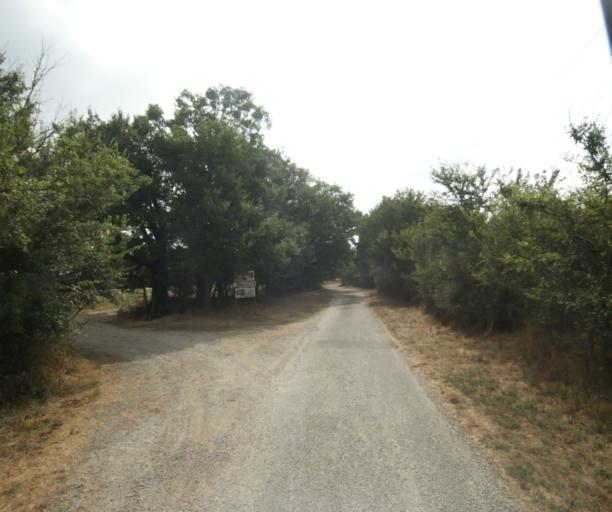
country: FR
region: Midi-Pyrenees
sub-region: Departement de la Haute-Garonne
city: Revel
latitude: 43.4418
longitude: 2.0011
